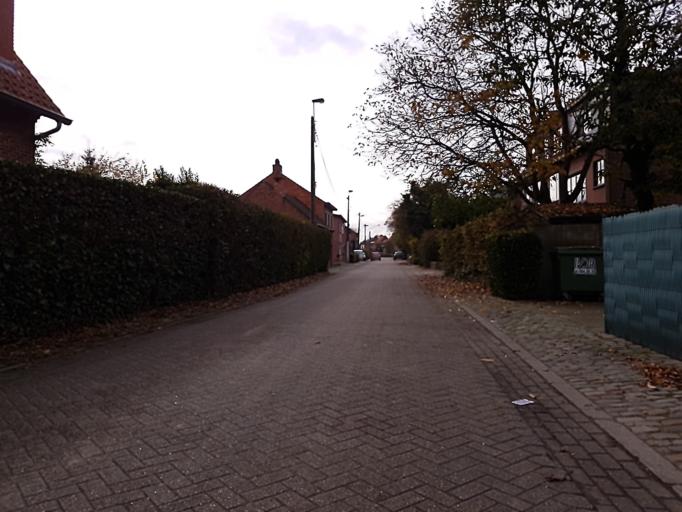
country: BE
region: Flanders
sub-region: Provincie Antwerpen
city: Ranst
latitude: 51.1848
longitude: 4.5471
